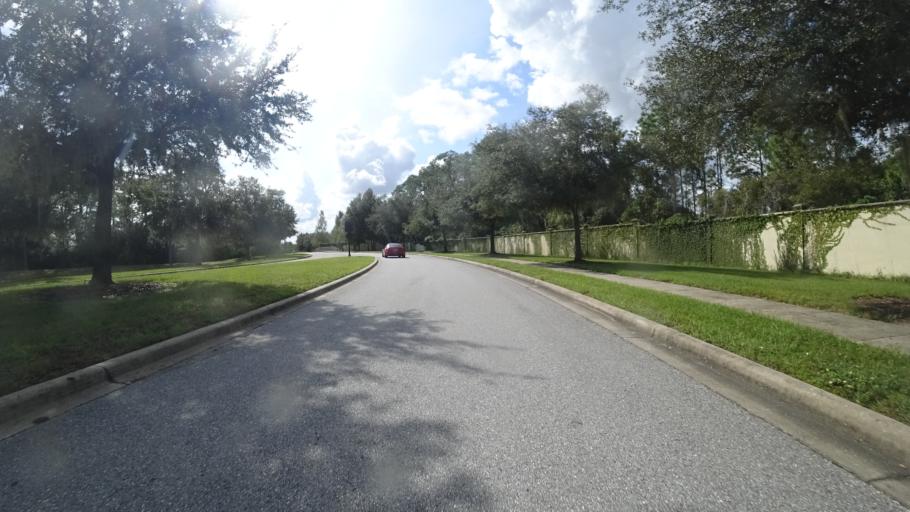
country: US
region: Florida
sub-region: Sarasota County
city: The Meadows
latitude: 27.4093
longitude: -82.3407
